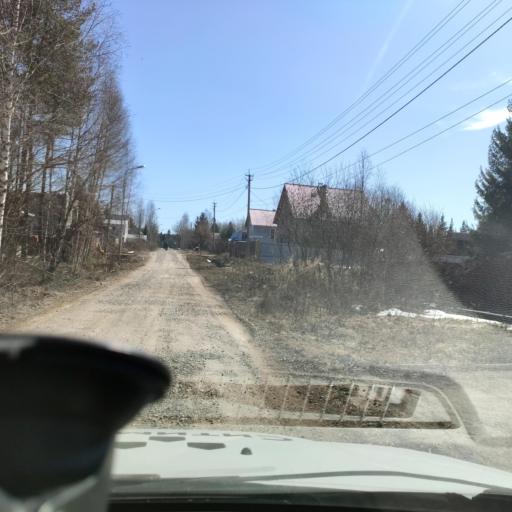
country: RU
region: Perm
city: Ferma
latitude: 57.9296
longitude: 56.4198
